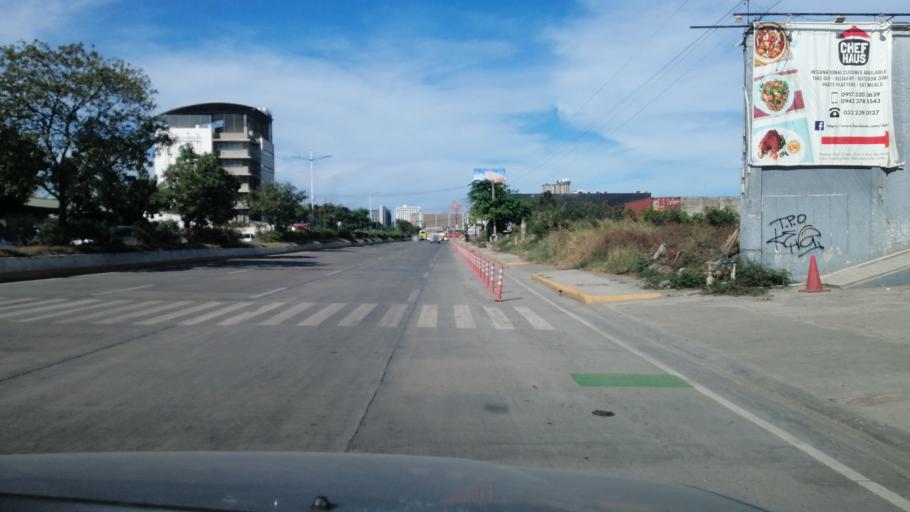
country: PH
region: Central Visayas
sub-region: Cebu City
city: Baugo
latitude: 10.3145
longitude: 123.9264
